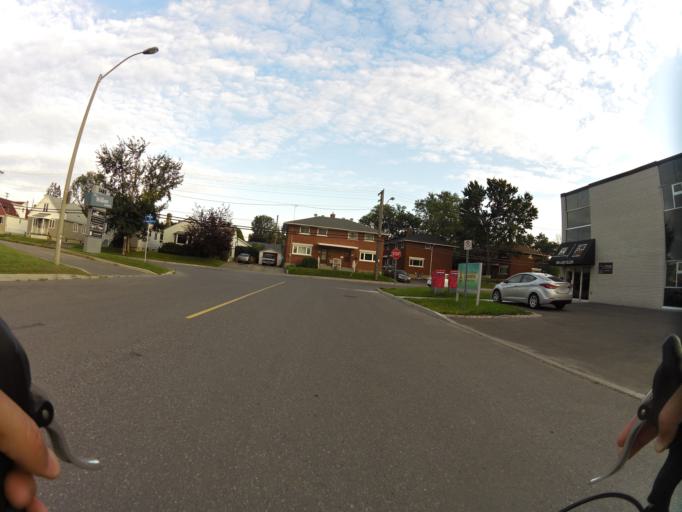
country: CA
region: Ontario
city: Ottawa
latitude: 45.3783
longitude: -75.7421
